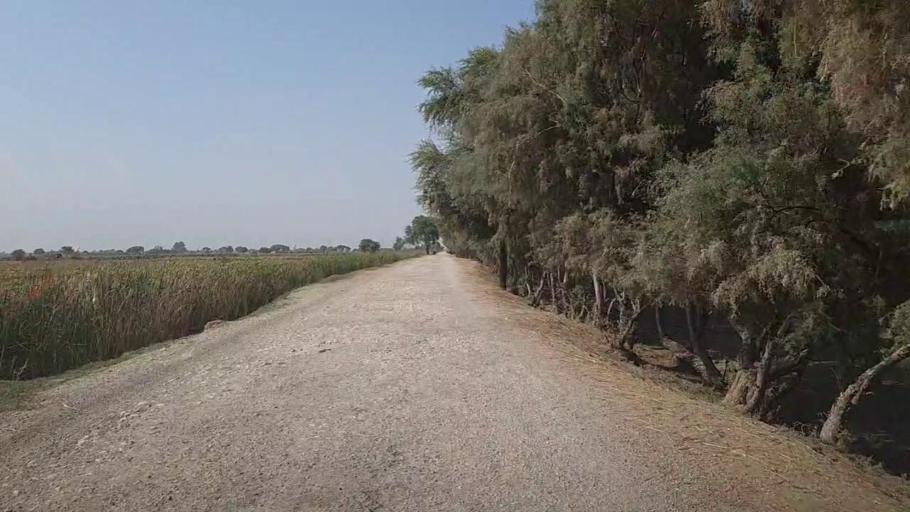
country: PK
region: Sindh
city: Kandhkot
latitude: 28.4031
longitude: 69.2592
